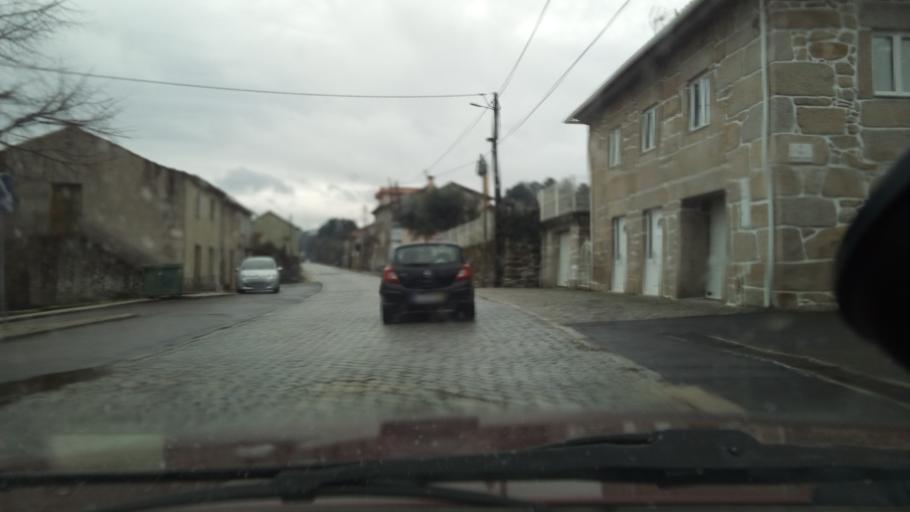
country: PT
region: Viseu
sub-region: Mangualde
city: Mangualde
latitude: 40.6098
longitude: -7.6563
